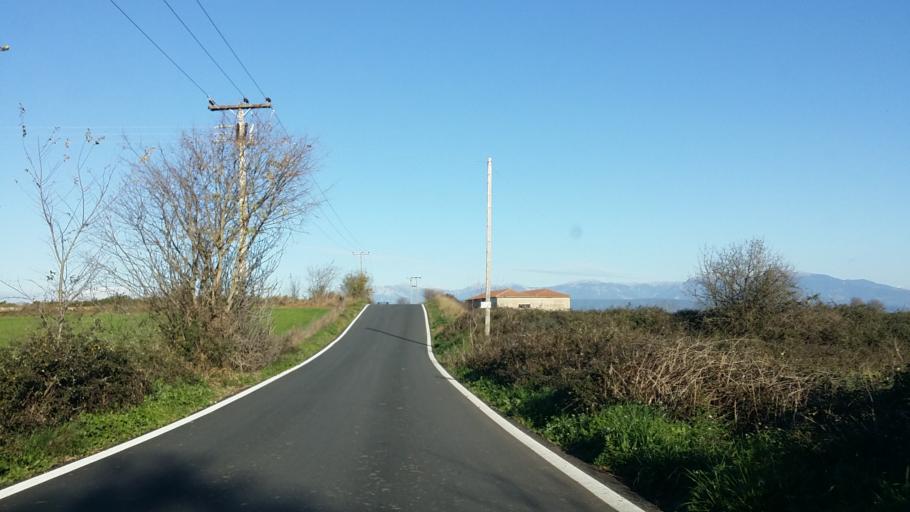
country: GR
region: West Greece
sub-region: Nomos Aitolias kai Akarnanias
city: Angelokastro
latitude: 38.6293
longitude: 21.2386
